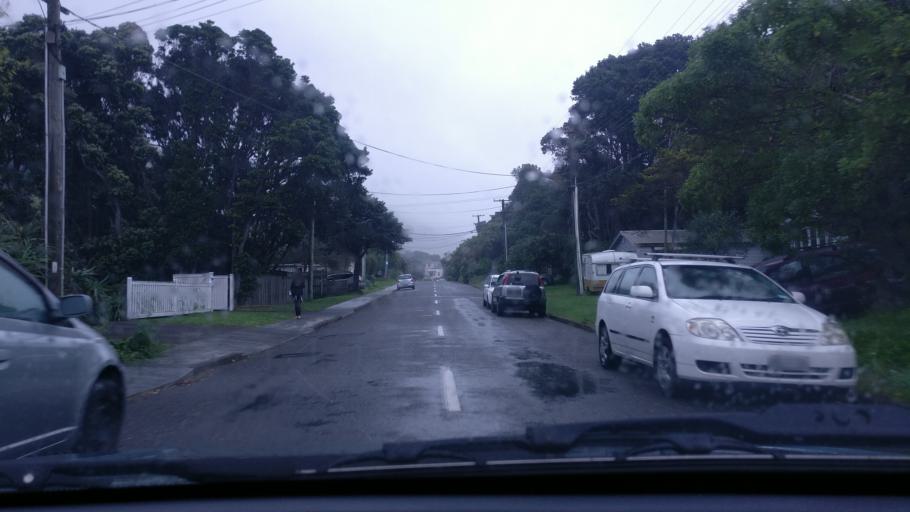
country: NZ
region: Wellington
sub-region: Kapiti Coast District
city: Paraparaumu
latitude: -40.9886
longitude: 174.9504
